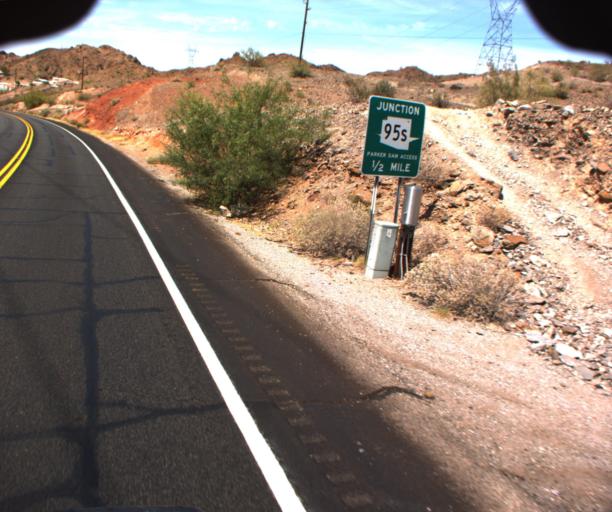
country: US
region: Arizona
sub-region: La Paz County
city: Cienega Springs
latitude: 34.2785
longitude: -114.1305
